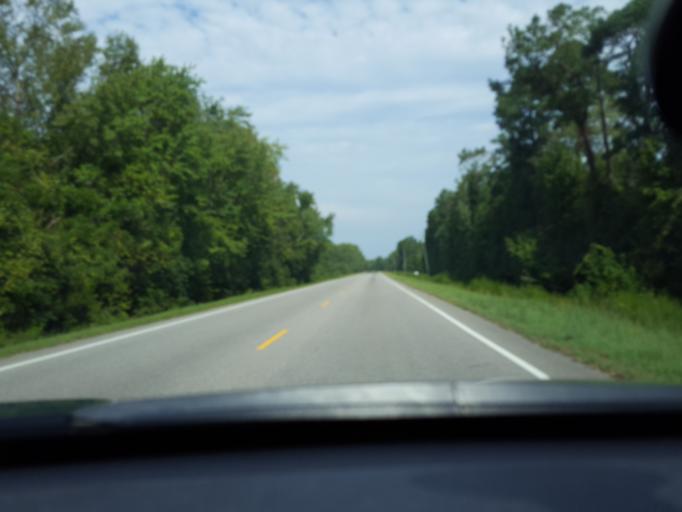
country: US
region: North Carolina
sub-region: Washington County
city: Plymouth
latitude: 35.9030
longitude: -76.7115
